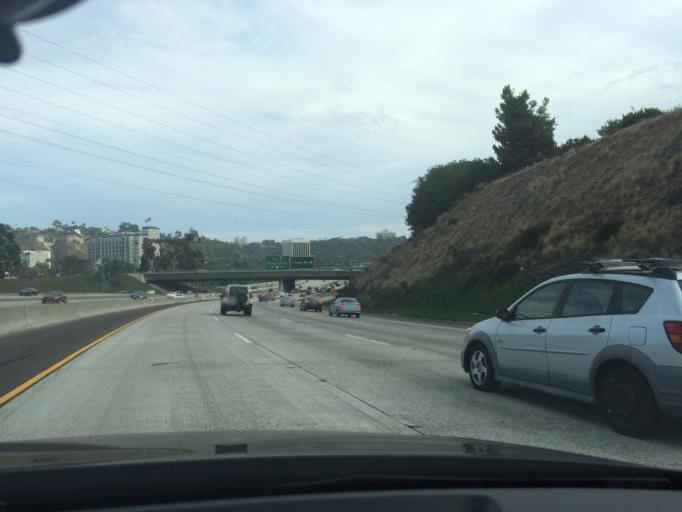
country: US
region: California
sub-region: San Diego County
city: San Diego
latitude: 32.7744
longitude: -117.1613
